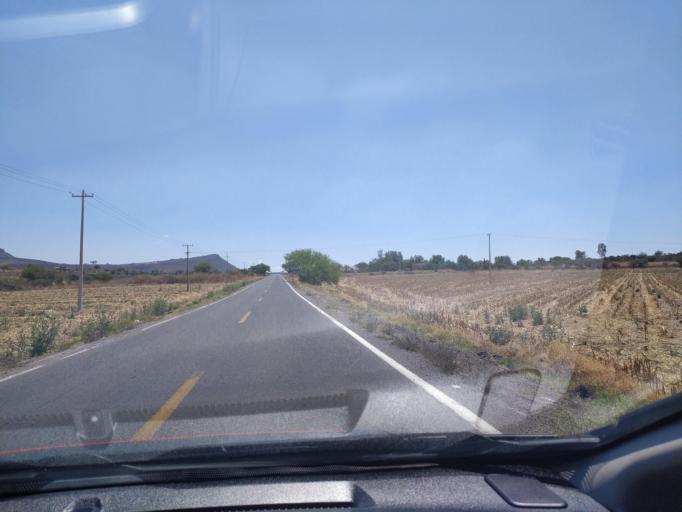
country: MX
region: Guanajuato
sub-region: San Francisco del Rincon
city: San Ignacio de Hidalgo
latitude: 20.8278
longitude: -101.8434
